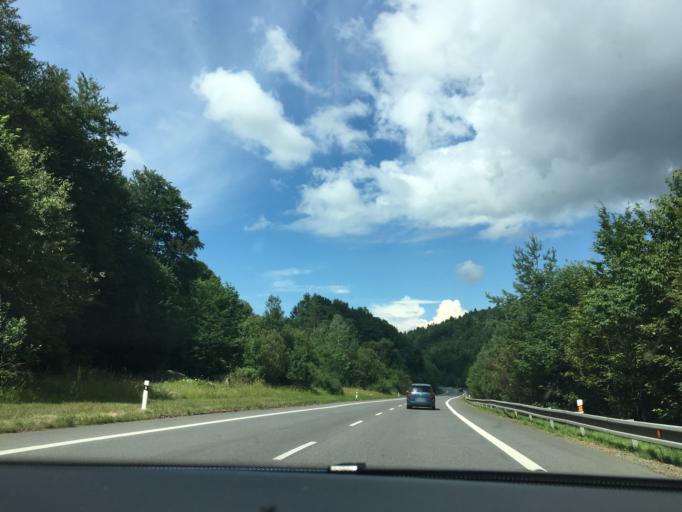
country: PL
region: Subcarpathian Voivodeship
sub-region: Powiat krosnienski
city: Jasliska
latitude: 49.3864
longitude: 21.6969
